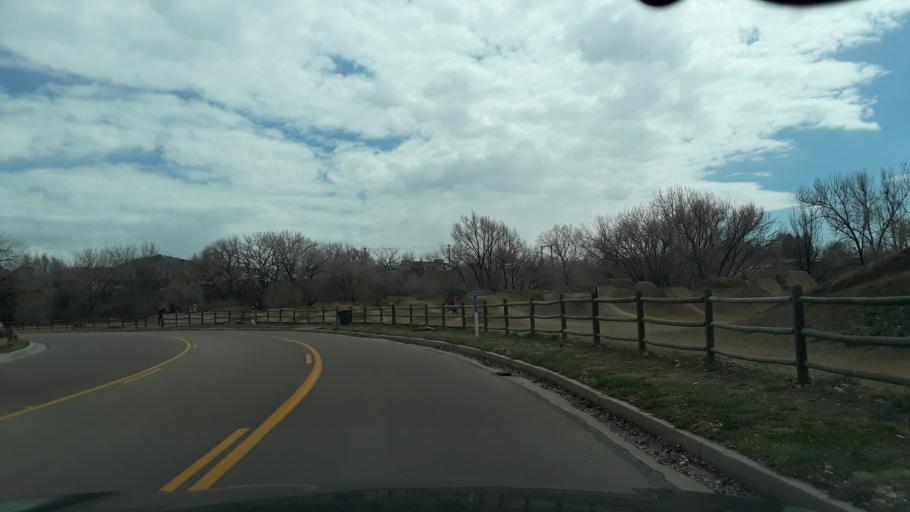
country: US
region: Colorado
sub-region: El Paso County
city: Colorado Springs
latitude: 38.8893
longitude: -104.8262
